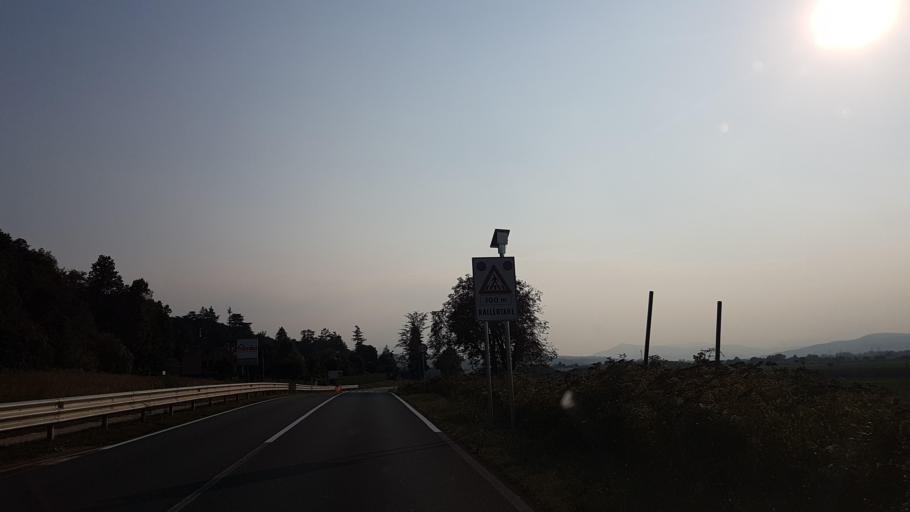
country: IT
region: Emilia-Romagna
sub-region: Provincia di Parma
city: Gaiano
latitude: 44.7342
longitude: 10.1869
